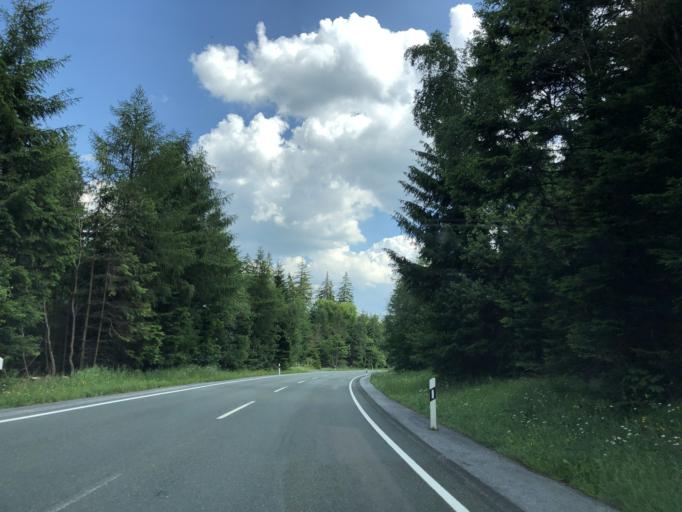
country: DE
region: North Rhine-Westphalia
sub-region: Regierungsbezirk Arnsberg
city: Bestwig
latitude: 51.4163
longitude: 8.4199
